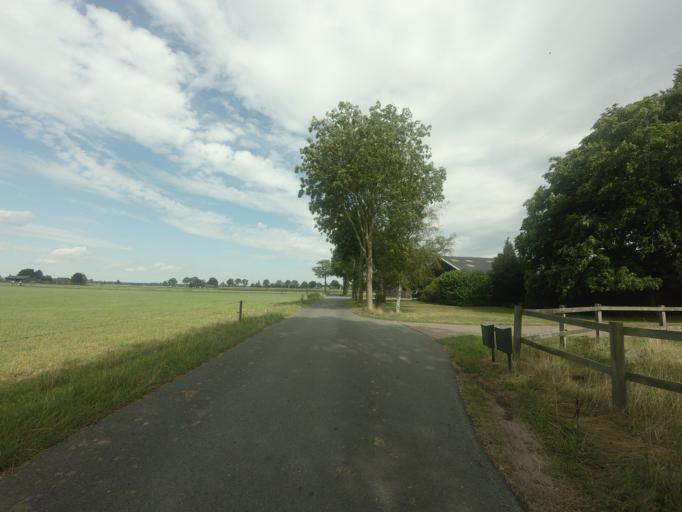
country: NL
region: Overijssel
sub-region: Gemeente Raalte
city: Raalte
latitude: 52.4609
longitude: 6.3604
